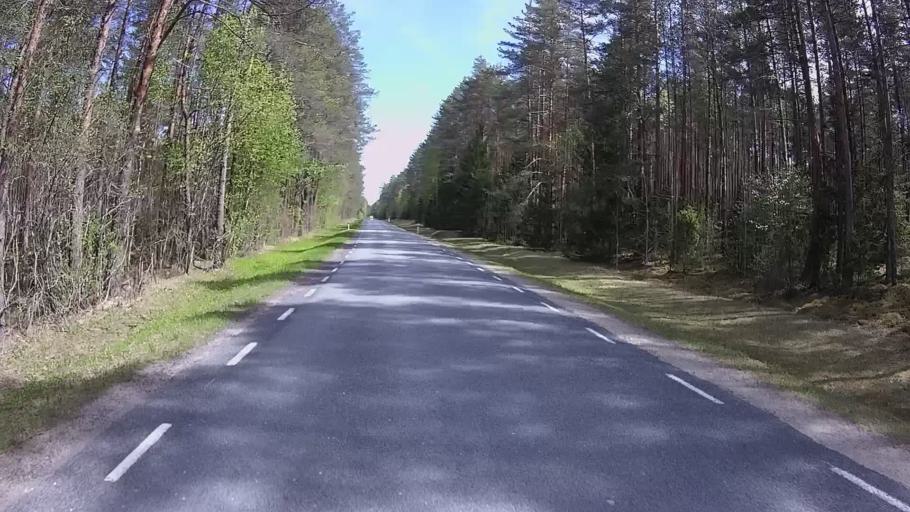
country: LV
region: Apes Novads
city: Ape
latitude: 57.6024
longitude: 26.4962
